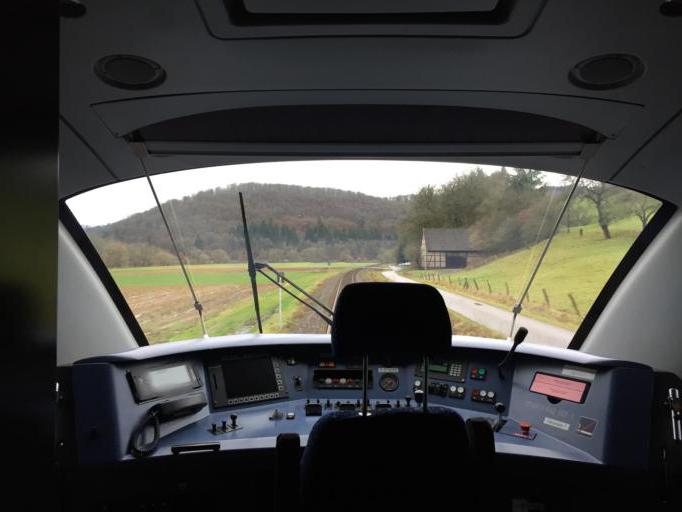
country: DE
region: Hesse
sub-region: Regierungsbezirk Kassel
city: Frankenau
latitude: 51.1219
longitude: 8.8718
